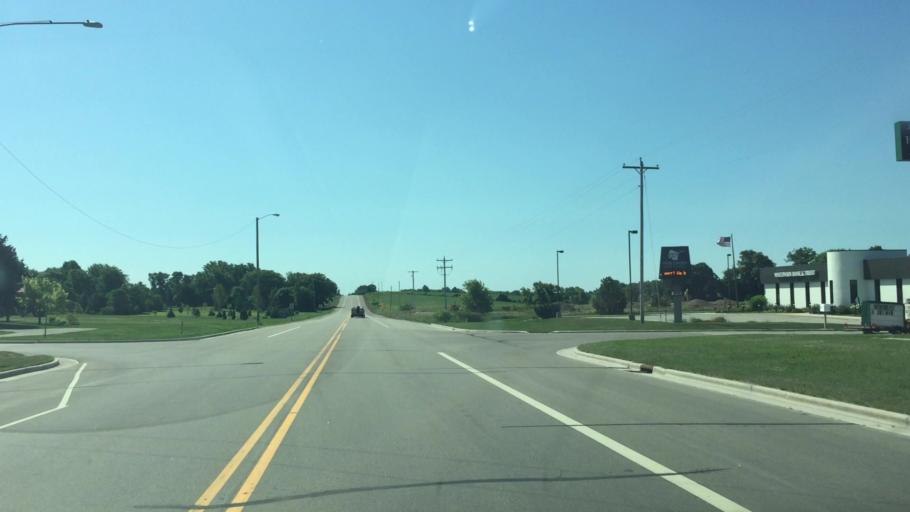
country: US
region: Wisconsin
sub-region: Calumet County
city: Chilton
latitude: 44.0180
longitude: -88.1507
